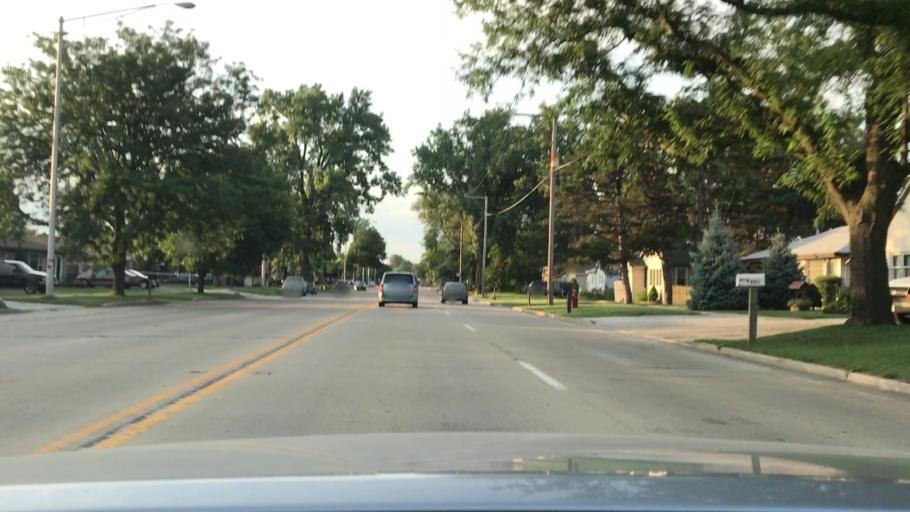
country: US
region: Illinois
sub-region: Cook County
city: Oak Lawn
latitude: 41.7294
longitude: -87.7606
